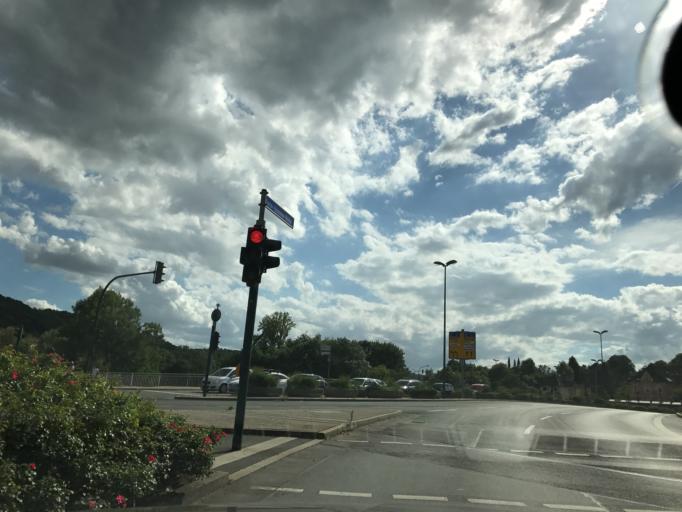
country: DE
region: North Rhine-Westphalia
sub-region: Regierungsbezirk Dusseldorf
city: Heiligenhaus
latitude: 51.3875
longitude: 7.0003
